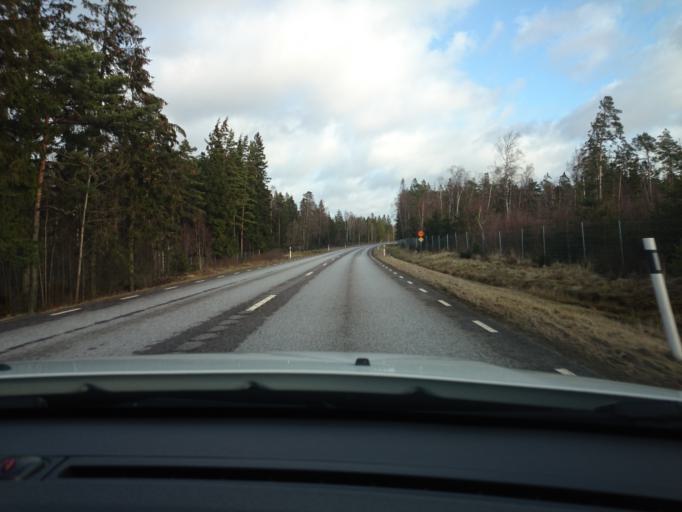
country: SE
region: Halland
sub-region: Hylte Kommun
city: Hyltebruk
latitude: 57.0300
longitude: 13.2720
